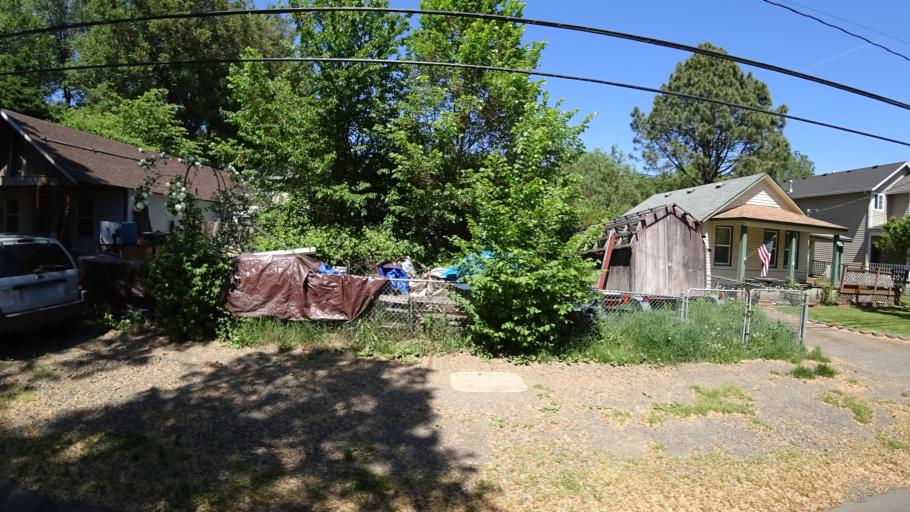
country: US
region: Oregon
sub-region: Washington County
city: Rockcreek
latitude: 45.5267
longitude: -122.9114
